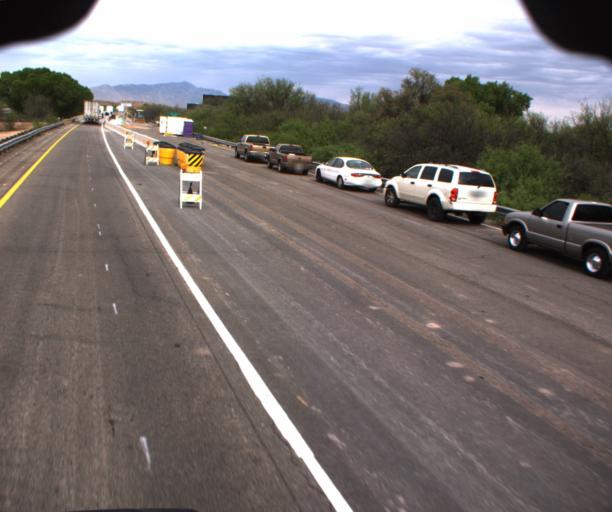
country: US
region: Arizona
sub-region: Cochise County
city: Benson
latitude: 31.9680
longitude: -110.2776
